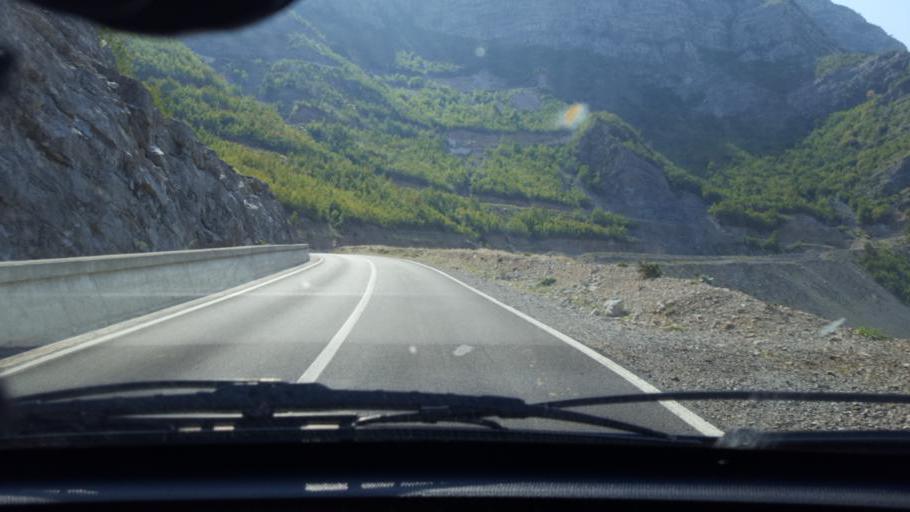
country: AL
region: Shkoder
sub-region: Rrethi i Malesia e Madhe
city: Kastrat
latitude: 42.4178
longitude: 19.5011
